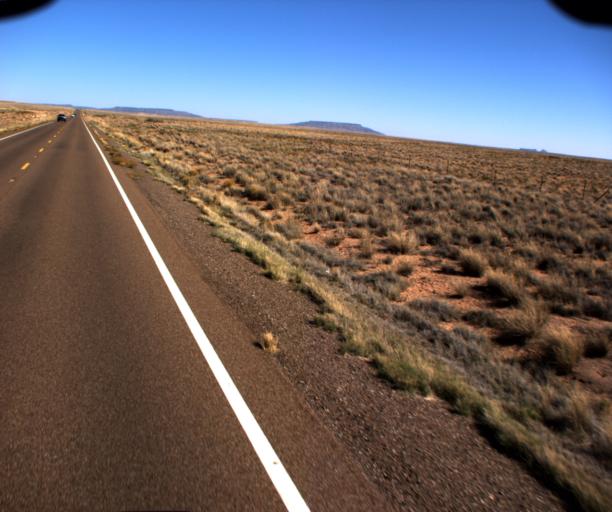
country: US
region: Arizona
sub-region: Navajo County
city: Winslow
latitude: 35.1294
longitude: -110.4980
